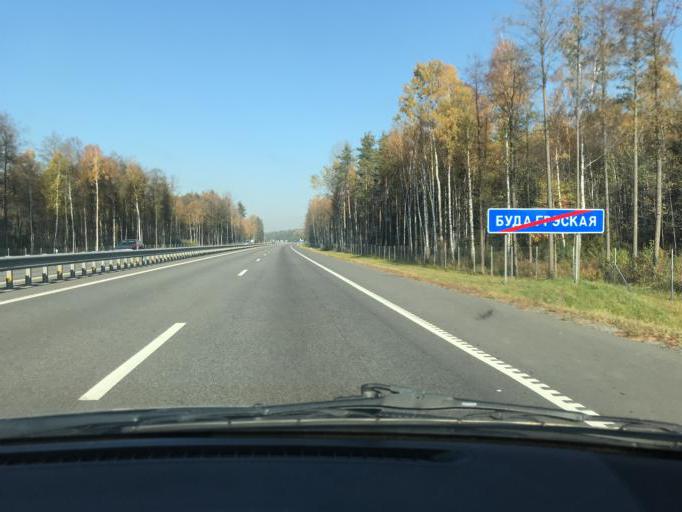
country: BY
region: Minsk
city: Slutsk
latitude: 53.2778
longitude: 27.5500
